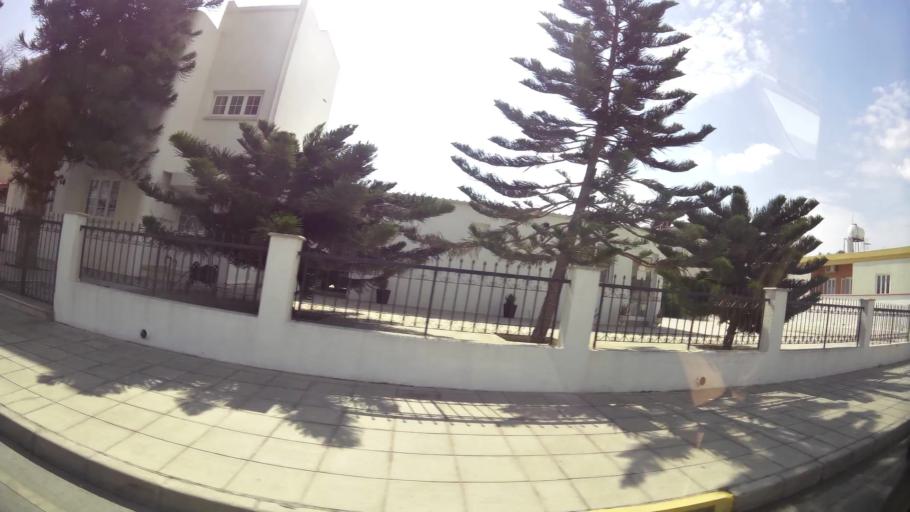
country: CY
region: Larnaka
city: Aradippou
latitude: 34.9514
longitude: 33.5819
